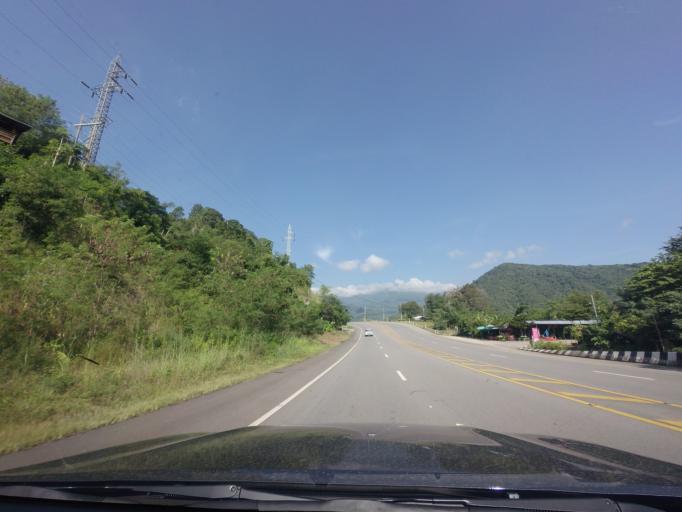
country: TH
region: Phetchabun
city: Lom Sak
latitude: 16.7788
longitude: 101.1095
